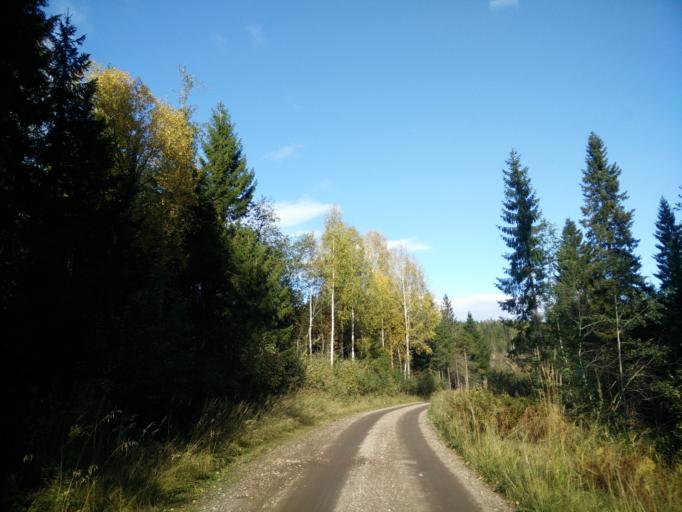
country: SE
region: Vaesternorrland
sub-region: Sundsvalls Kommun
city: Matfors
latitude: 62.3293
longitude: 16.9091
